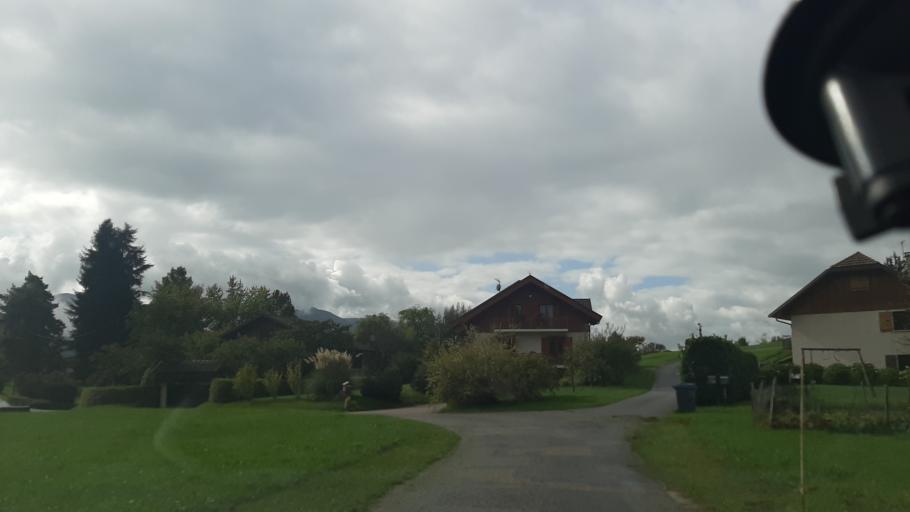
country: FR
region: Rhone-Alpes
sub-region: Departement de la Savoie
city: Gresy-sur-Isere
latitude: 45.6074
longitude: 6.2686
